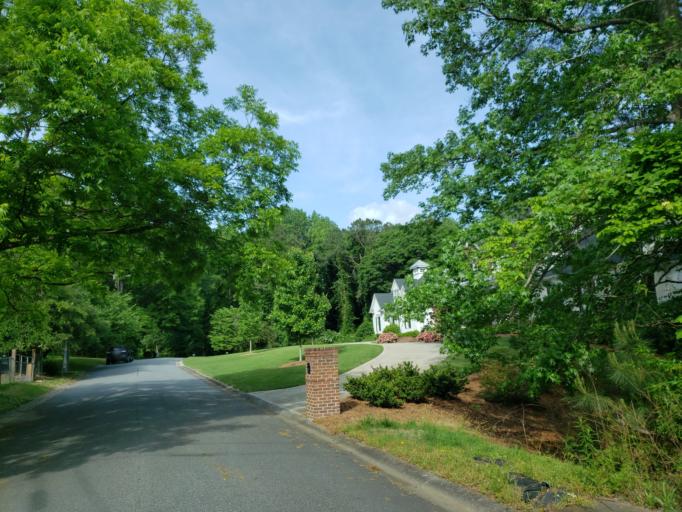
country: US
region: Georgia
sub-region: Cobb County
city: Marietta
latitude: 33.9499
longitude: -84.5669
